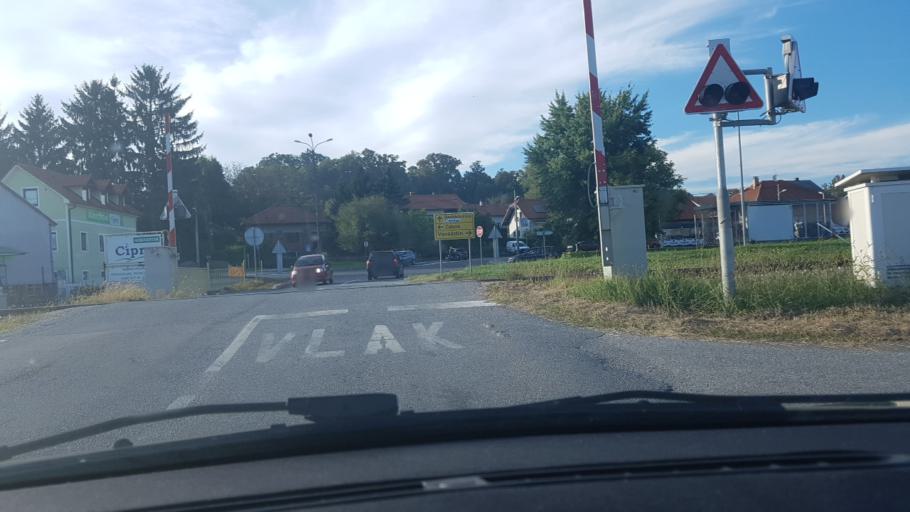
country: HR
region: Krapinsko-Zagorska
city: Bedekovcina
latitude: 46.0395
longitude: 15.9922
